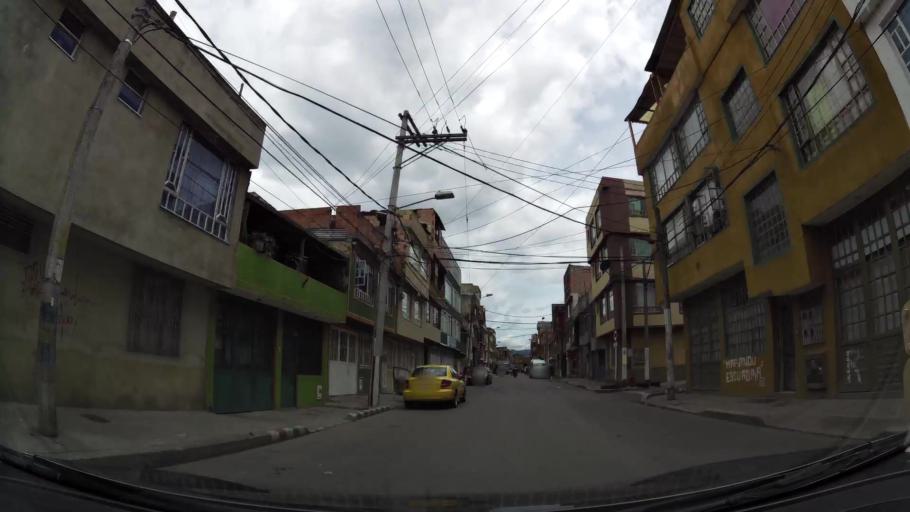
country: CO
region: Cundinamarca
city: Funza
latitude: 4.7080
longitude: -74.1327
